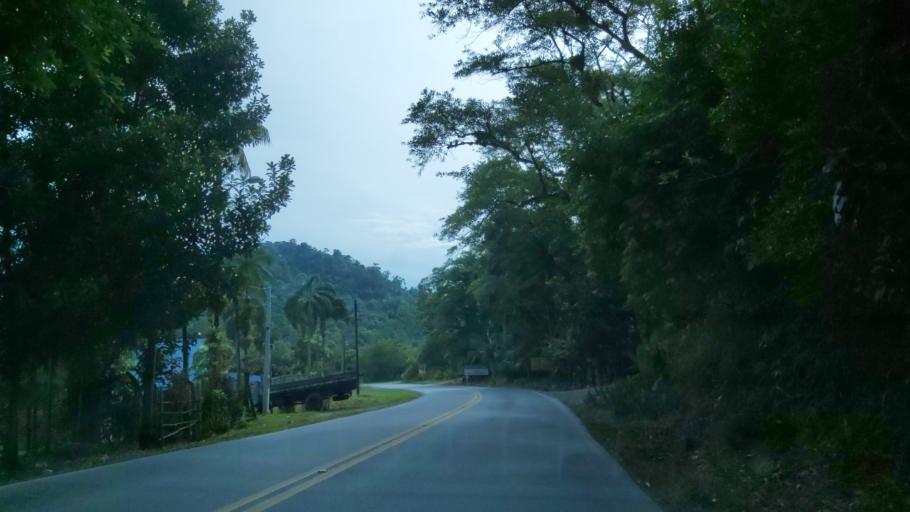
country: BR
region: Sao Paulo
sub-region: Miracatu
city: Miracatu
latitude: -24.0650
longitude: -47.5938
